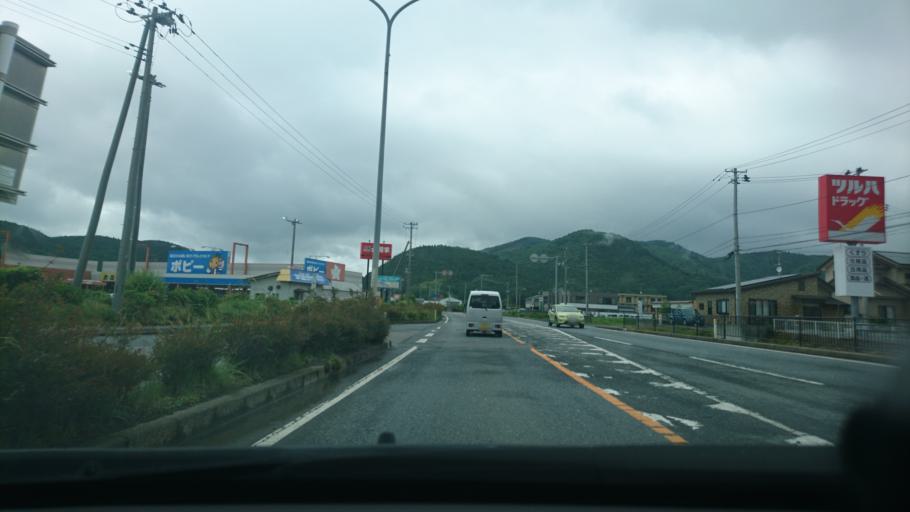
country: JP
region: Miyagi
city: Ishinomaki
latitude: 38.5236
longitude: 141.3122
